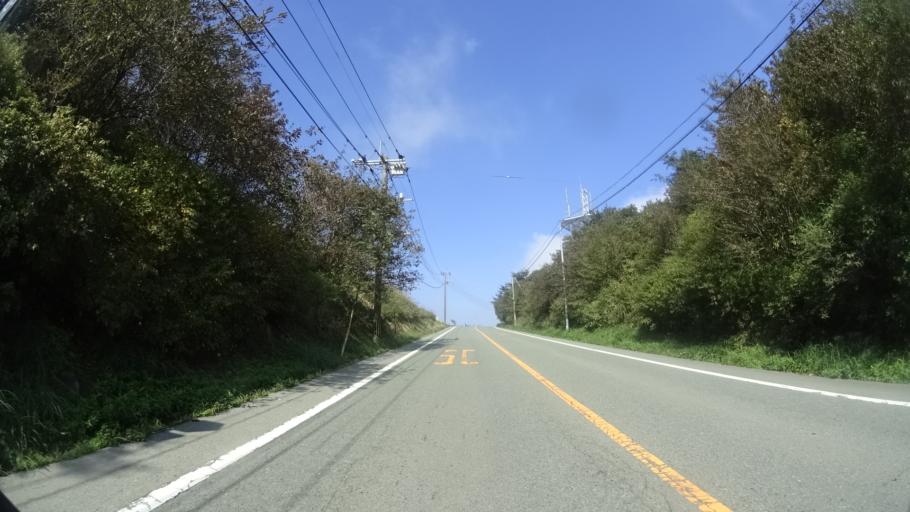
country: JP
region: Kumamoto
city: Aso
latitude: 32.9372
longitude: 130.9720
